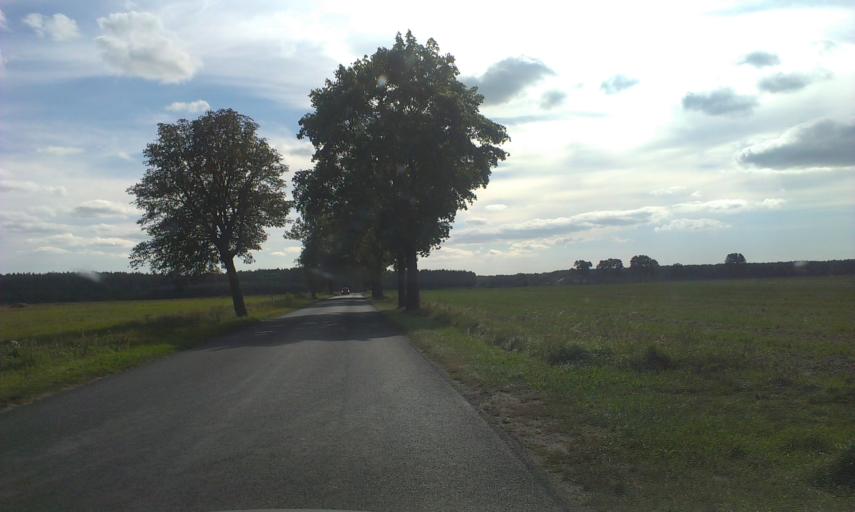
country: PL
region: Greater Poland Voivodeship
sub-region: Powiat zlotowski
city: Zlotow
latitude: 53.3262
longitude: 17.0890
